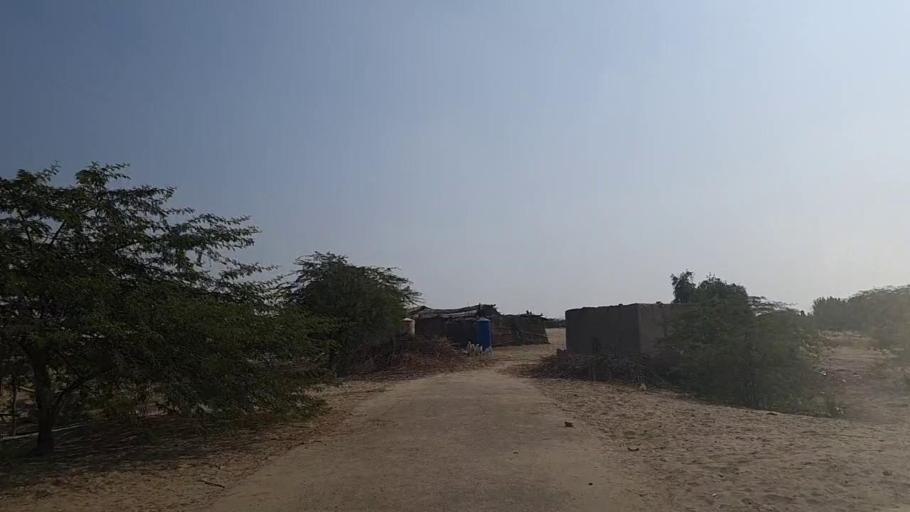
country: PK
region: Sindh
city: Daur
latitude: 26.4654
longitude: 68.4578
